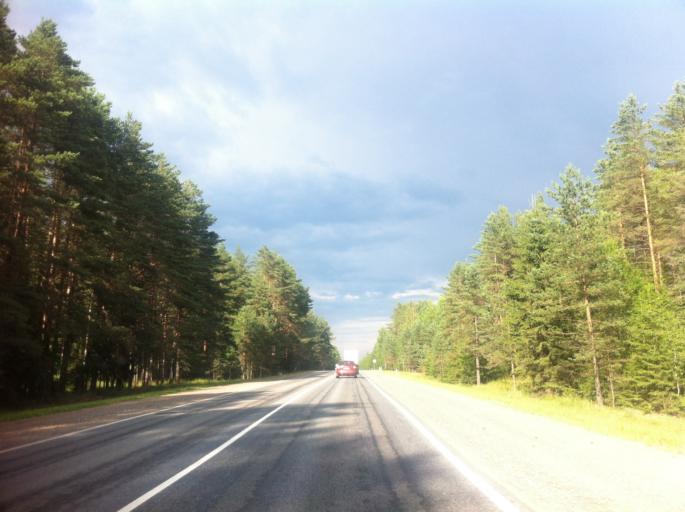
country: RU
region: Pskov
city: Strugi-Krasnyye
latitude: 58.2056
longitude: 29.3095
